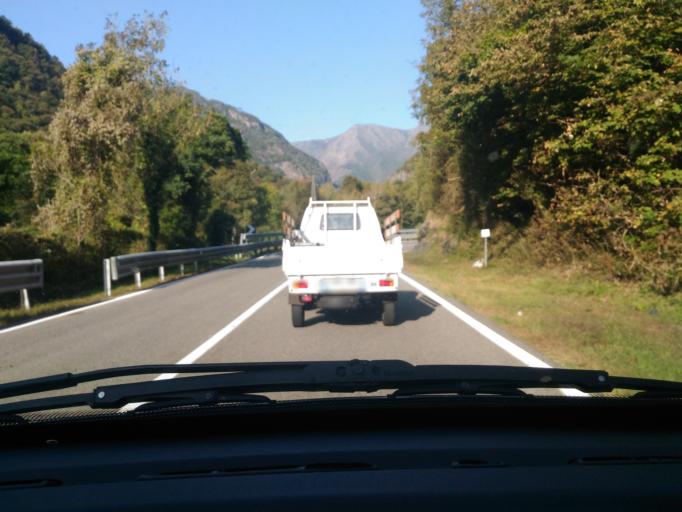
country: IT
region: Piedmont
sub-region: Provincia di Vercelli
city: Varallo
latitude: 45.8192
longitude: 8.2315
